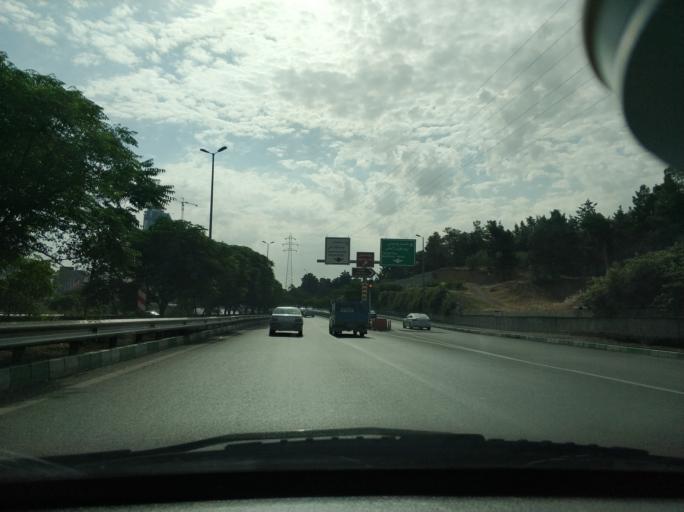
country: IR
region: Tehran
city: Tehran
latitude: 35.7215
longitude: 51.5202
